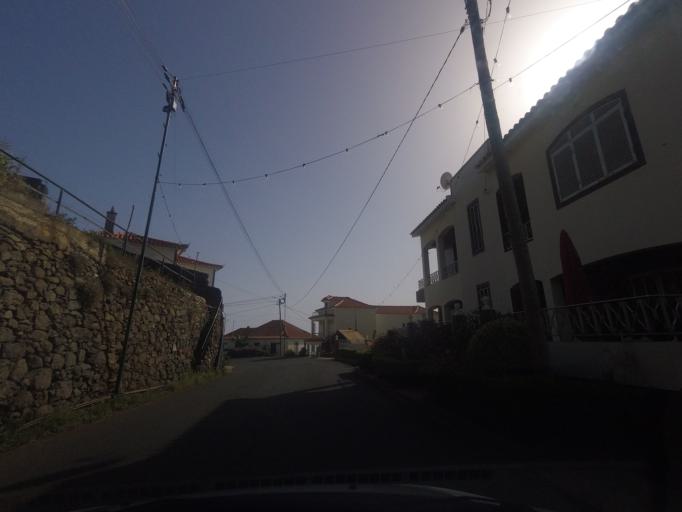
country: PT
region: Madeira
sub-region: Calheta
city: Arco da Calheta
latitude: 32.7273
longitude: -17.1536
